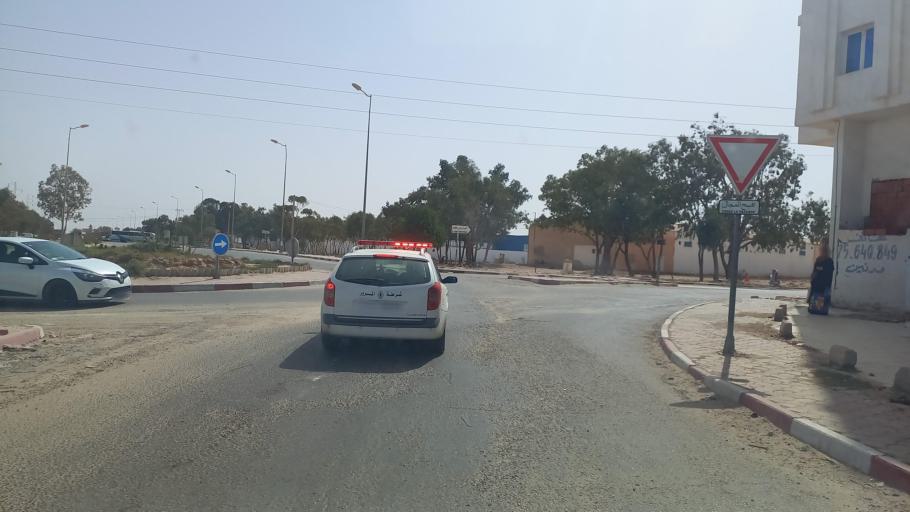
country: TN
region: Madanin
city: Medenine
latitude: 33.3419
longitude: 10.5056
